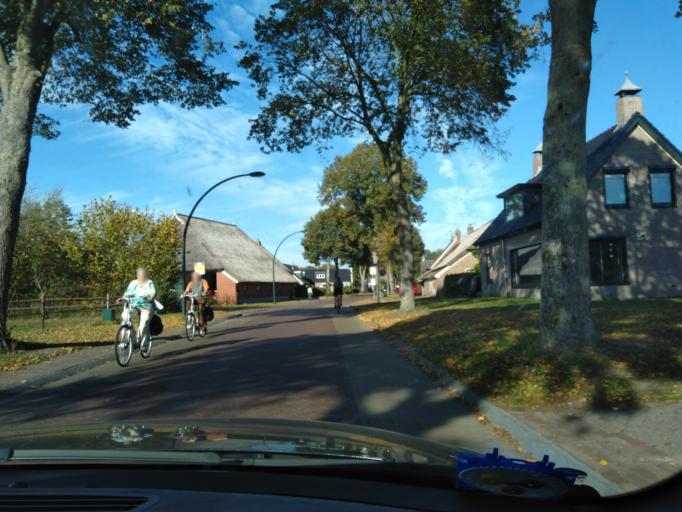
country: NL
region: Drenthe
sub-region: Gemeente Aa en Hunze
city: Anloo
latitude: 53.0330
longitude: 6.6617
